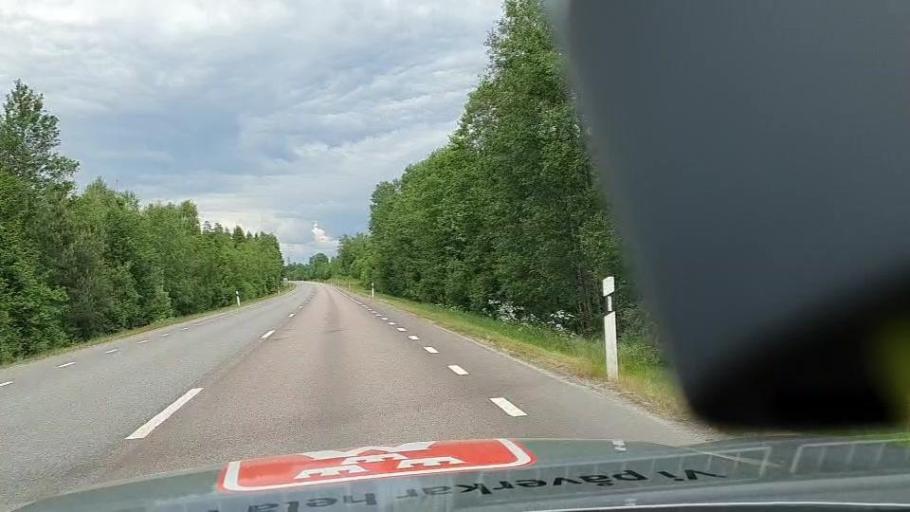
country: SE
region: Kalmar
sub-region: Emmaboda Kommun
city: Emmaboda
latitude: 56.4399
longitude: 15.5517
